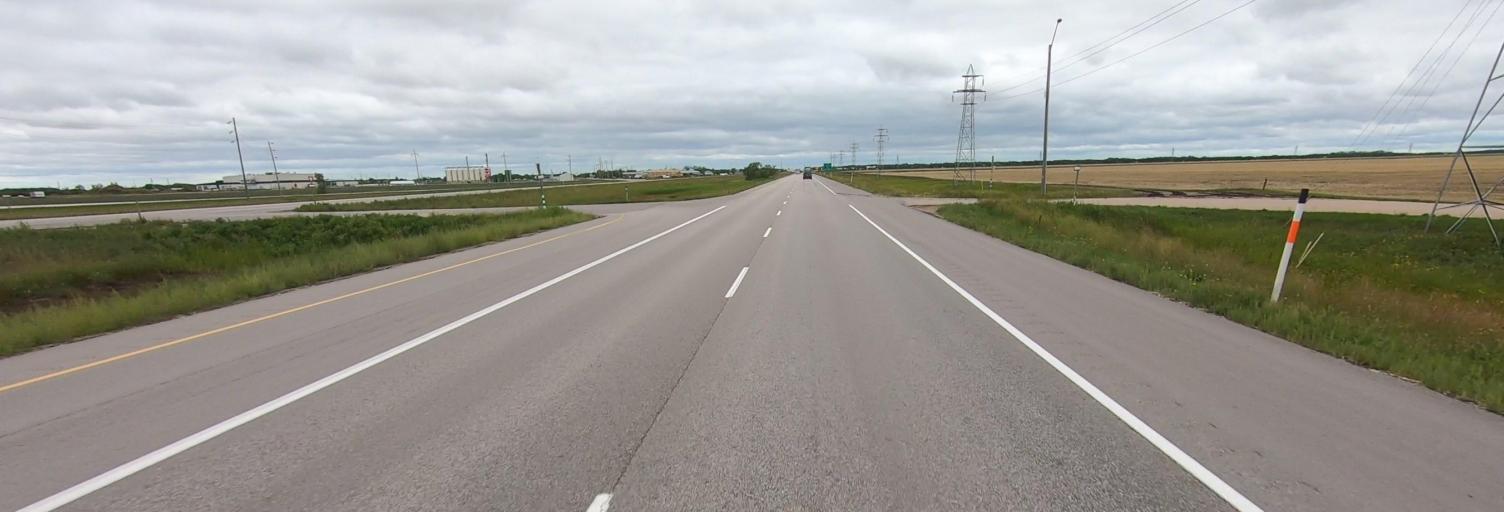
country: CA
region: Manitoba
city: Headingley
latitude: 49.9016
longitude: -97.7255
